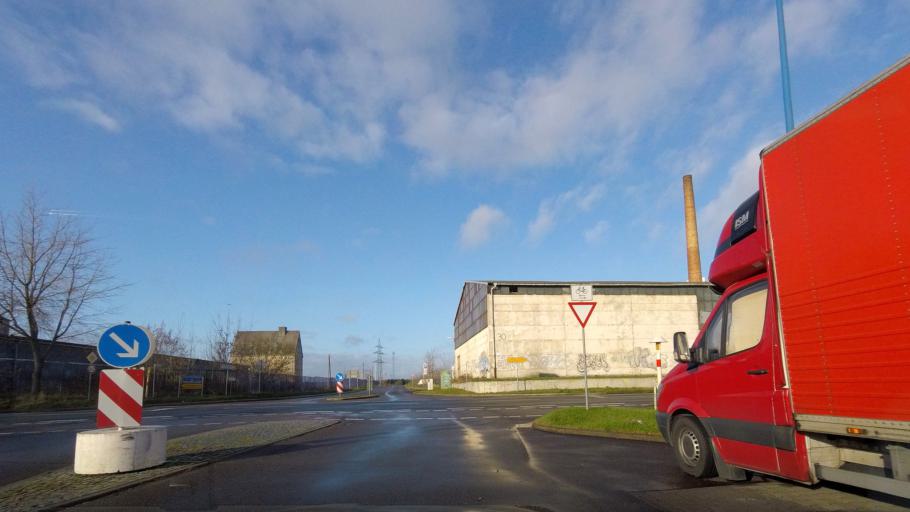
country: DE
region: Brandenburg
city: Niemegk
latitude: 52.0810
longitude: 12.7066
